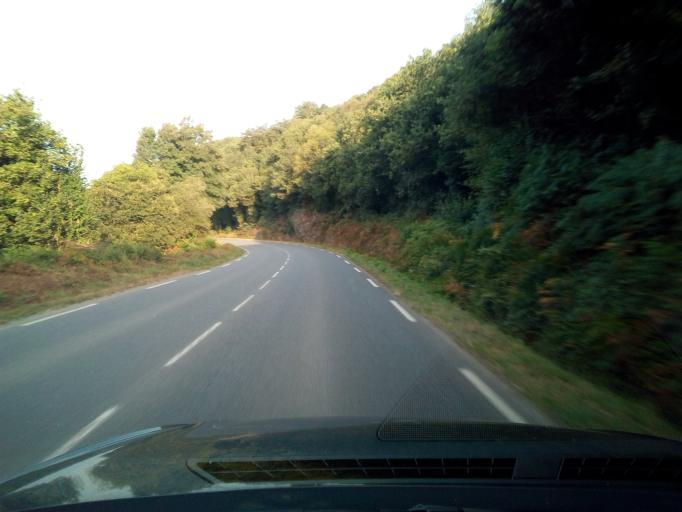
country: FR
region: Brittany
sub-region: Departement du Finistere
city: Bodilis
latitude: 48.4871
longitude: -4.1406
